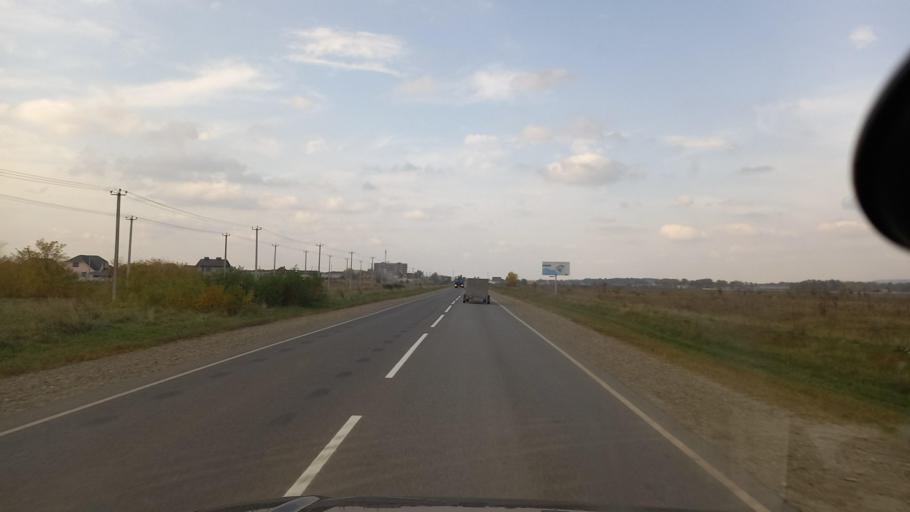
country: RU
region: Krasnodarskiy
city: Mostovskoy
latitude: 44.3839
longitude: 40.8196
